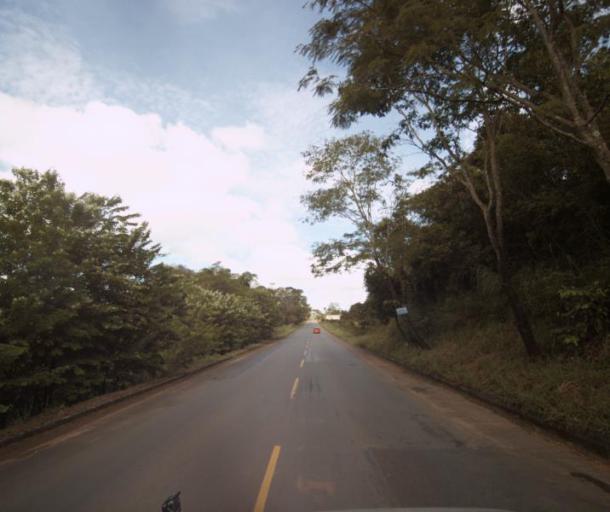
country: BR
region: Goias
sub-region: Pirenopolis
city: Pirenopolis
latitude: -15.8791
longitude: -48.7882
